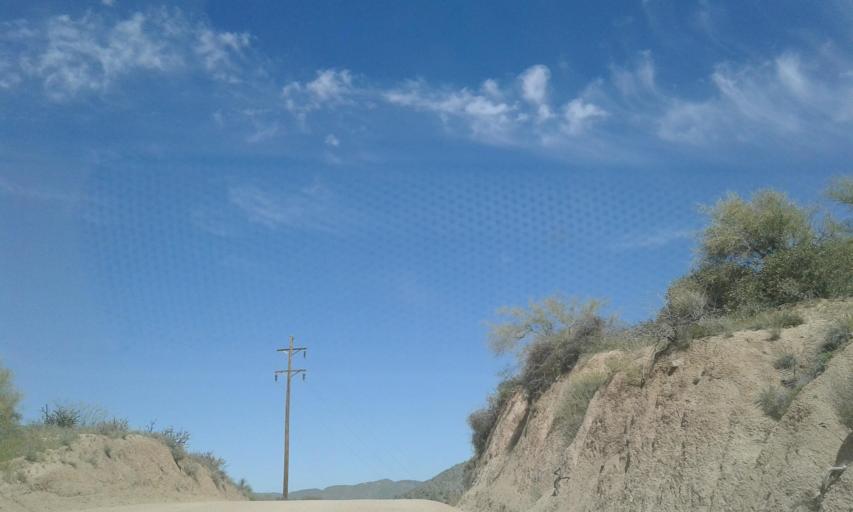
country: US
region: Arizona
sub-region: Gila County
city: Tonto Basin
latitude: 33.5868
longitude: -111.2113
